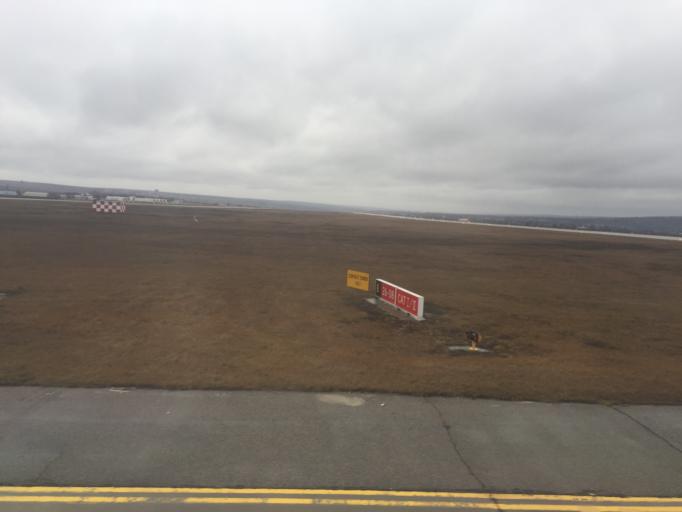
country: MD
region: Chisinau
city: Singera
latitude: 46.9290
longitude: 28.9342
